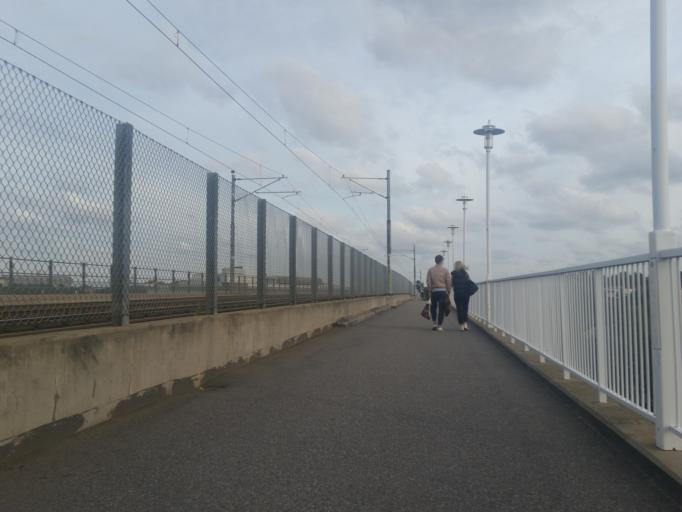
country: SE
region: Stockholm
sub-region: Solna Kommun
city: Solna
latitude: 59.3267
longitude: 17.9858
